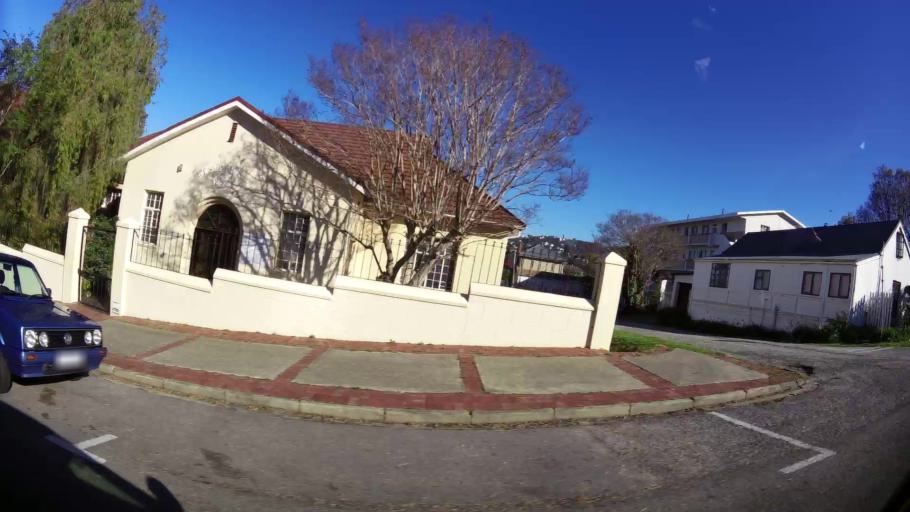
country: ZA
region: Western Cape
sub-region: Eden District Municipality
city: Knysna
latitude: -34.0346
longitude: 23.0523
